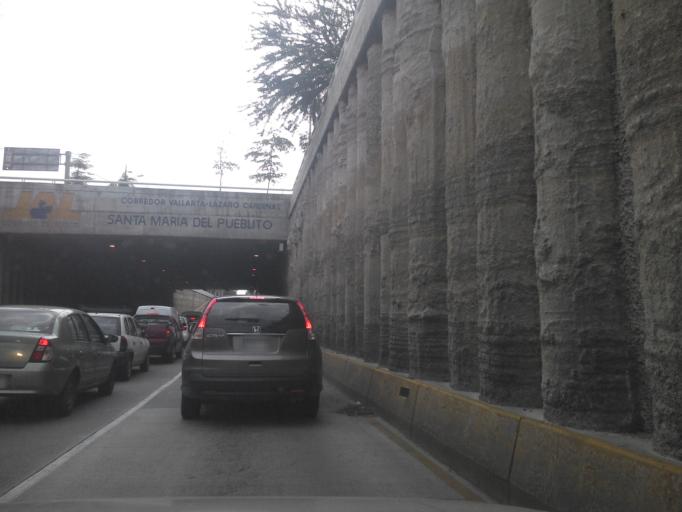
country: MX
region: Jalisco
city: Guadalajara
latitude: 20.6820
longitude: -103.4360
